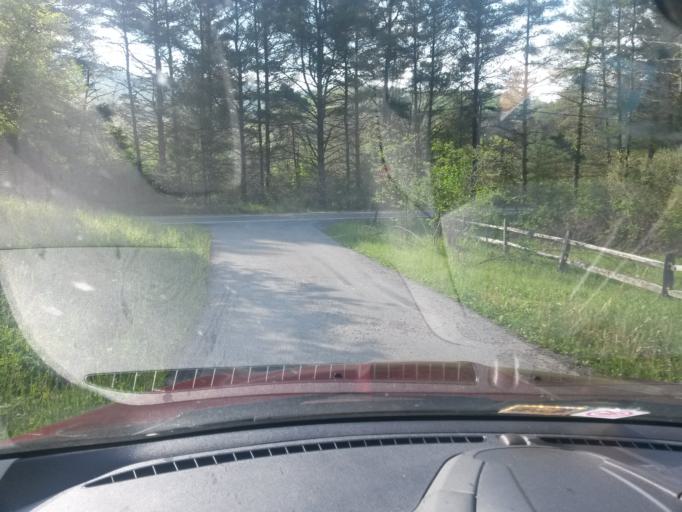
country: US
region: West Virginia
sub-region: Pocahontas County
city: Marlinton
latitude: 38.0349
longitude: -80.0347
